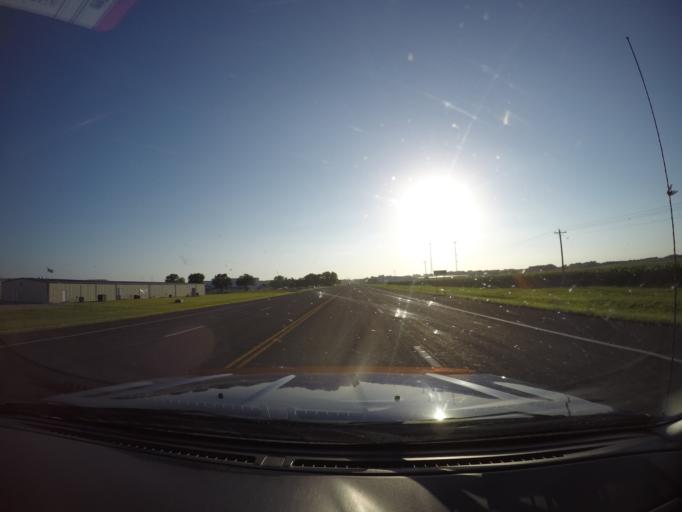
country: US
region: Kansas
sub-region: Pottawatomie County
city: Wamego
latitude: 39.2100
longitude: -96.2871
